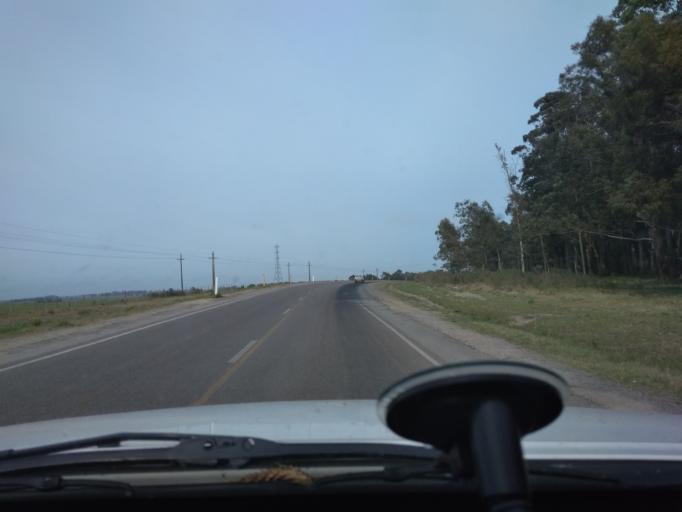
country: UY
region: Florida
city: Florida
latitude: -34.1028
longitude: -56.1139
